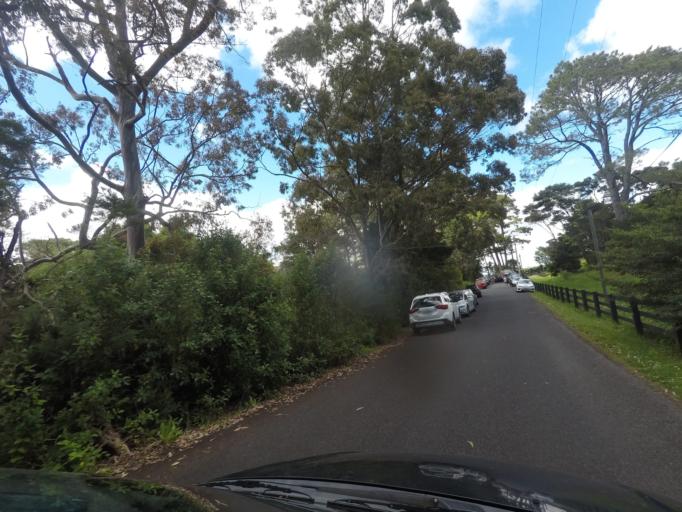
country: NZ
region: Auckland
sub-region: Auckland
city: Rothesay Bay
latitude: -36.7661
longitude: 174.6410
